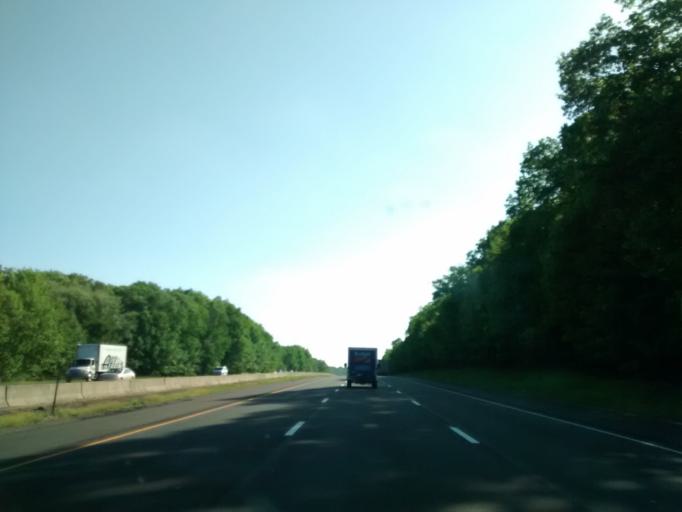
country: US
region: Connecticut
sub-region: Tolland County
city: Stafford Springs
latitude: 41.9311
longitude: -72.2456
